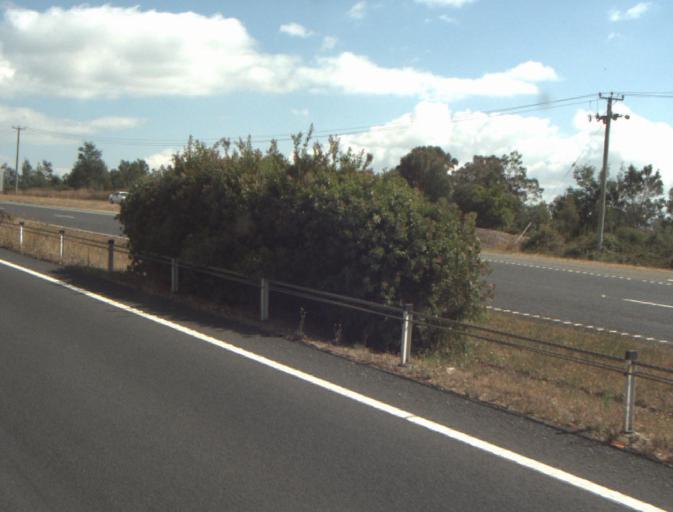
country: AU
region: Tasmania
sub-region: Launceston
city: Summerhill
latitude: -41.4791
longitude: 147.1481
